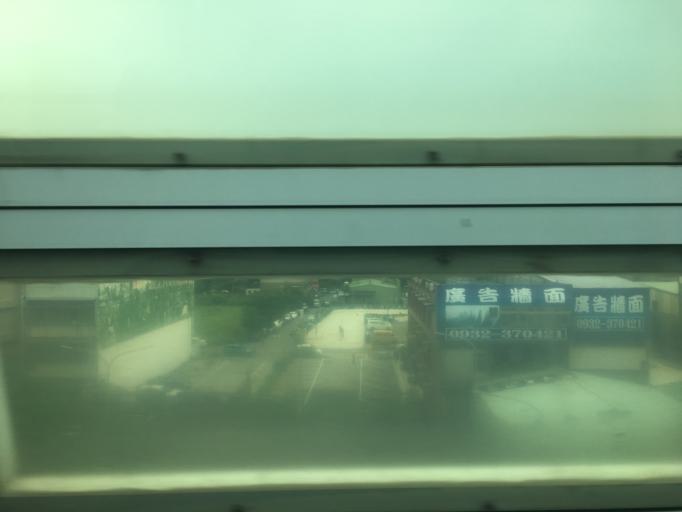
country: TW
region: Taiwan
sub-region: Taoyuan
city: Taoyuan
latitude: 25.0593
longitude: 121.3718
